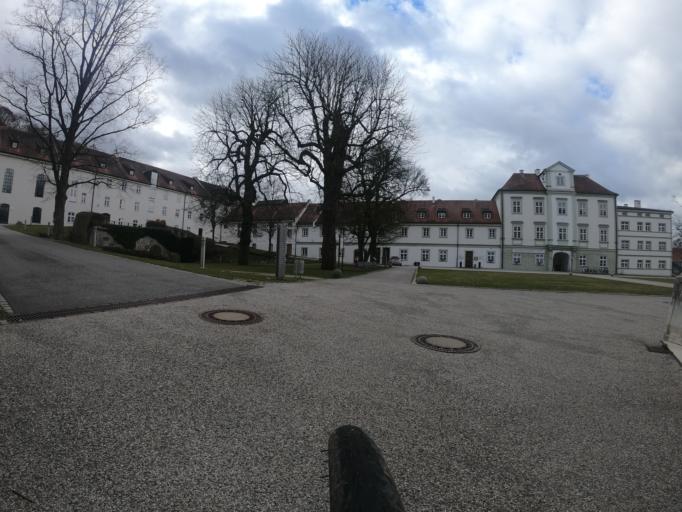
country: DE
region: Bavaria
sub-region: Upper Bavaria
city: Fuerstenfeldbruck
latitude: 48.1695
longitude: 11.2498
